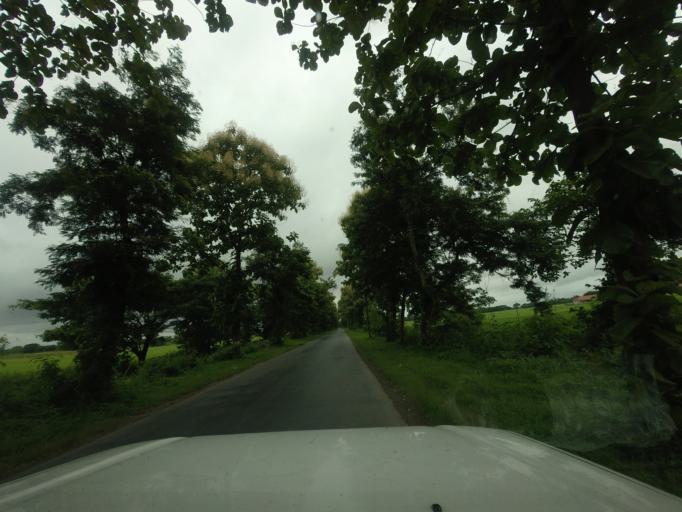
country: MM
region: Ayeyarwady
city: Hinthada
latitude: 17.6135
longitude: 95.4804
